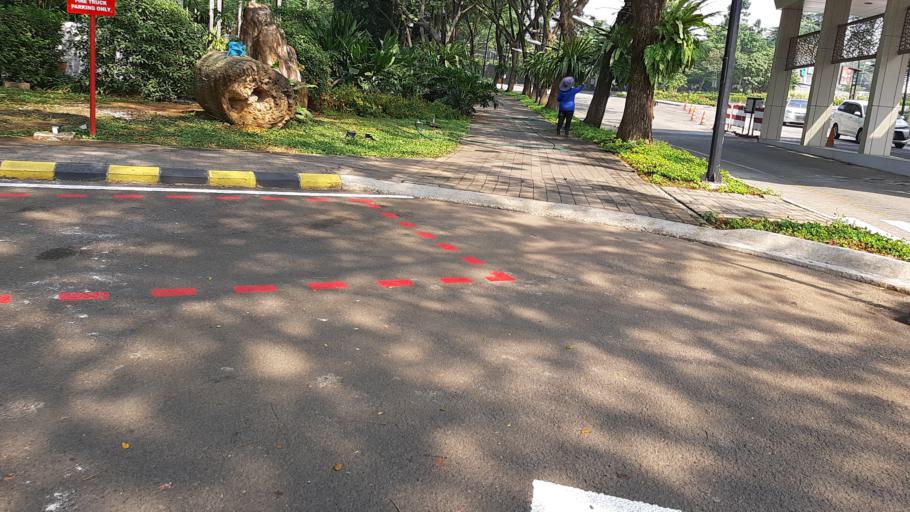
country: ID
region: West Java
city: Serpong
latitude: -6.3005
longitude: 106.6521
